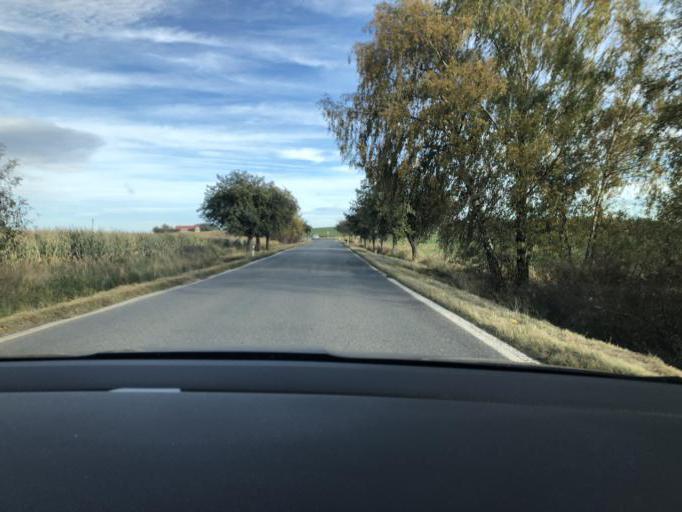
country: CZ
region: Central Bohemia
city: Divisov
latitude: 49.7881
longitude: 14.8554
